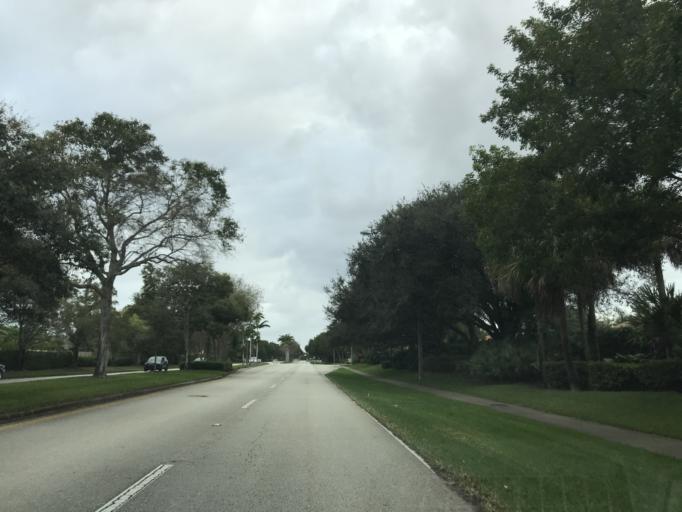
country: US
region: Florida
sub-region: Broward County
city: Parkland
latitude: 26.2981
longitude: -80.2595
